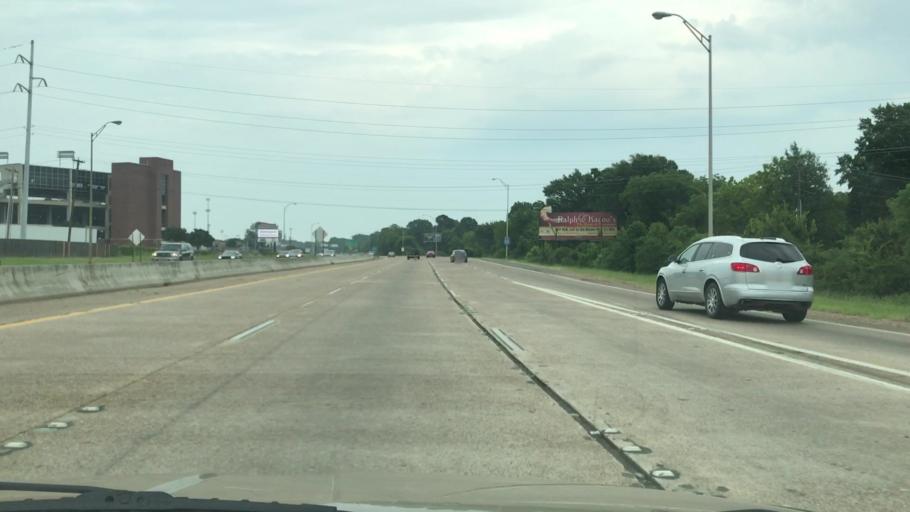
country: US
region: Louisiana
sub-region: Caddo Parish
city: Shreveport
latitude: 32.4728
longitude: -93.7950
